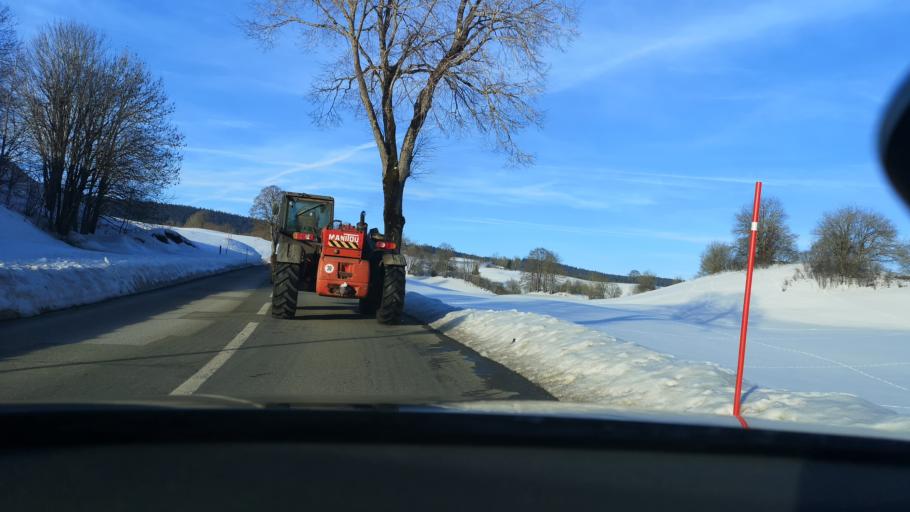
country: CH
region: Neuchatel
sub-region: Val-de-Travers District
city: Fleurier
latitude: 46.9073
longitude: 6.4998
